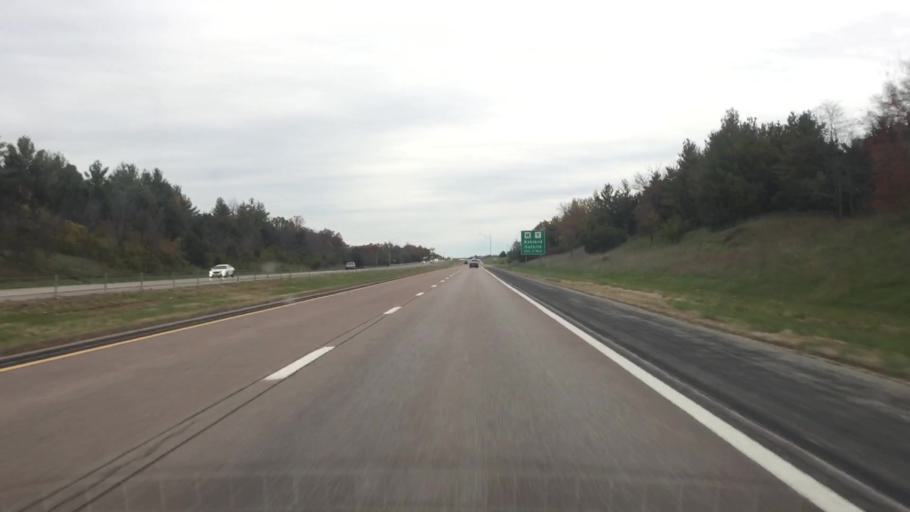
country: US
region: Missouri
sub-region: Boone County
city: Ashland
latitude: 38.7558
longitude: -92.2529
